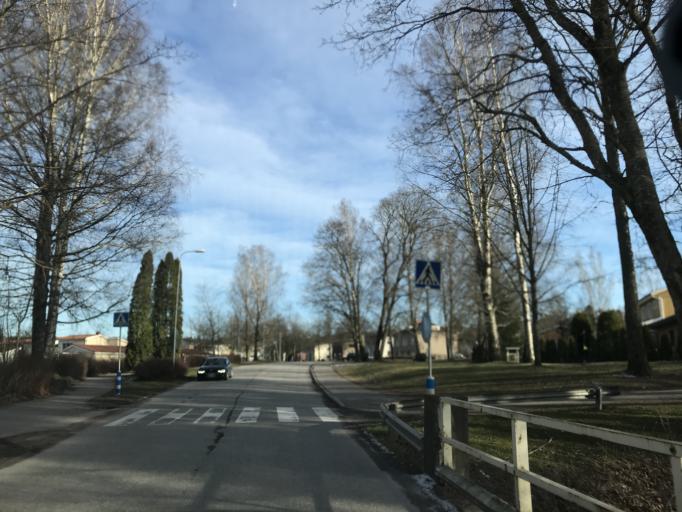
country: FI
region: Uusimaa
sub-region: Raaseporin
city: Karis
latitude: 60.0769
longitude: 23.6790
